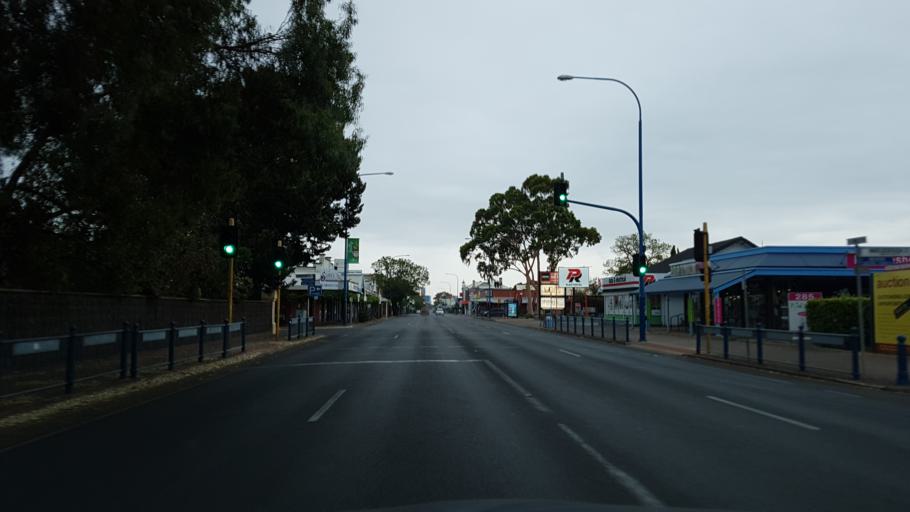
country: AU
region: South Australia
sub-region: Unley
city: Unley Park
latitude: -34.9588
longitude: 138.6081
